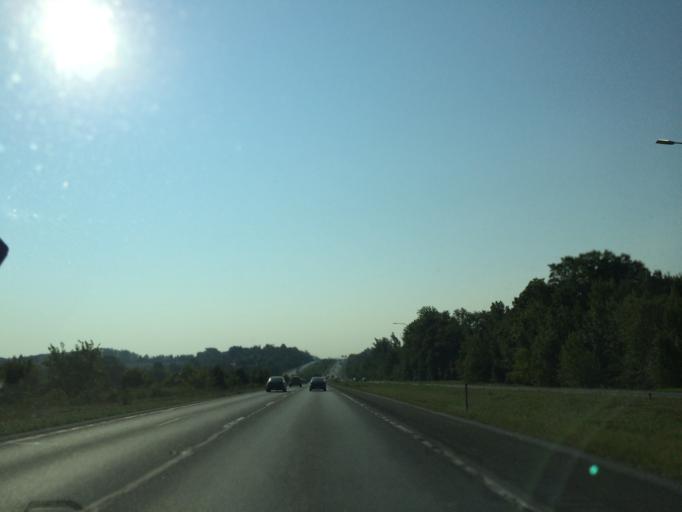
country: US
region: Maryland
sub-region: Howard County
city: Savage
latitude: 39.1379
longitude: -76.8113
